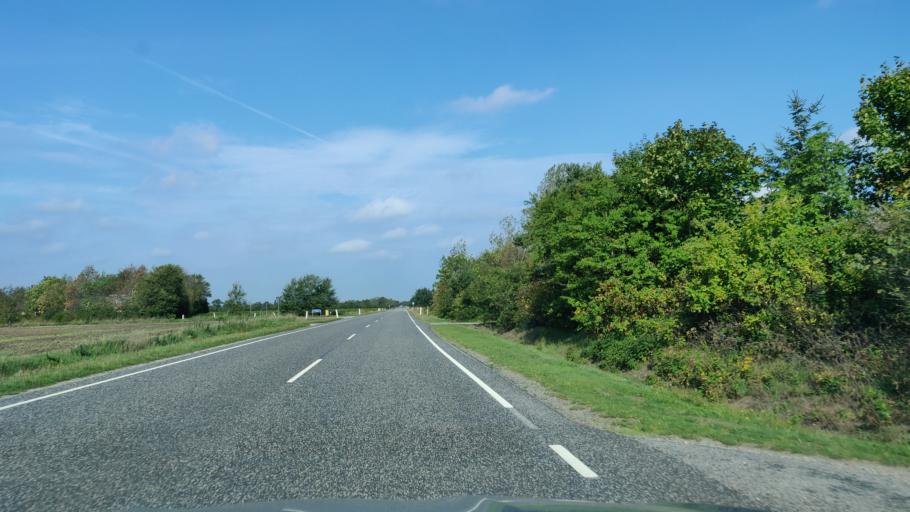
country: DK
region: Central Jutland
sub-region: Herning Kommune
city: Sunds
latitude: 56.2492
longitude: 9.0617
